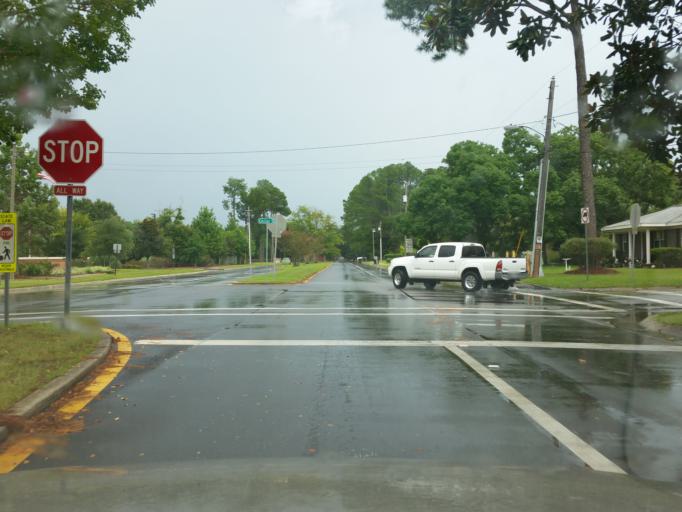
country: US
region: Florida
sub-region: Escambia County
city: Ferry Pass
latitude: 30.4878
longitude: -87.2154
